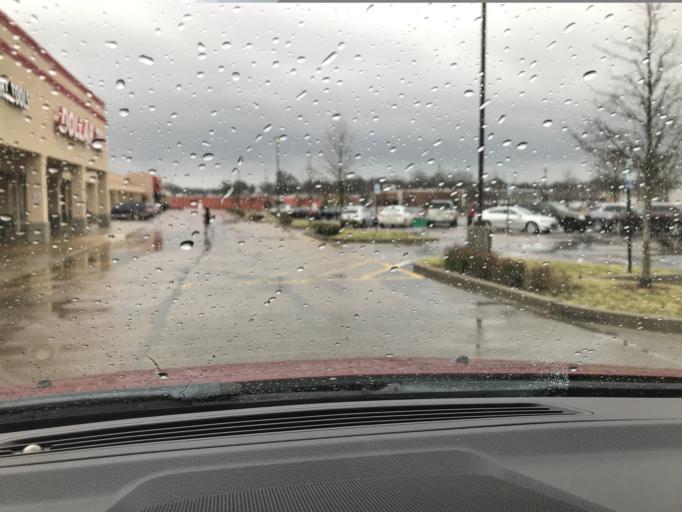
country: US
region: Tennessee
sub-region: Shelby County
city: Collierville
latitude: 35.0462
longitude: -89.6865
